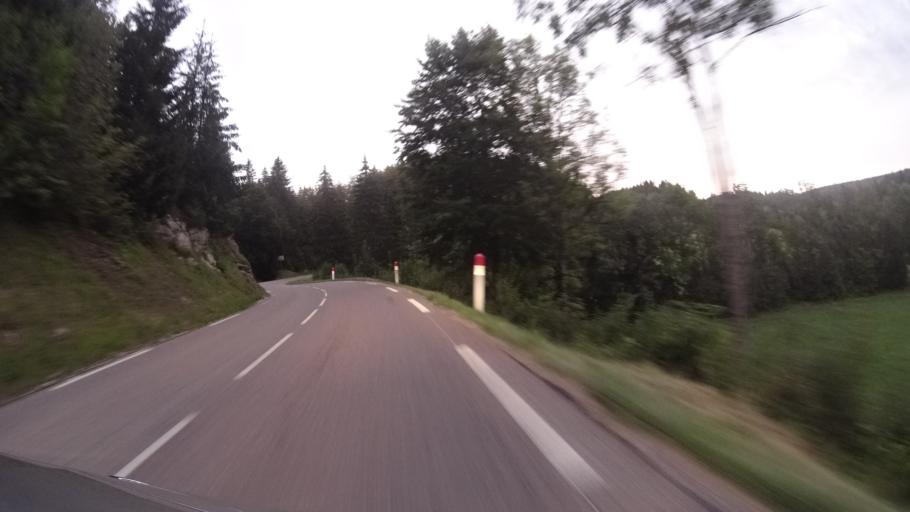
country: CH
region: Vaud
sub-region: Jura-Nord vaudois District
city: Le Chenit
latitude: 46.6687
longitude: 6.0934
